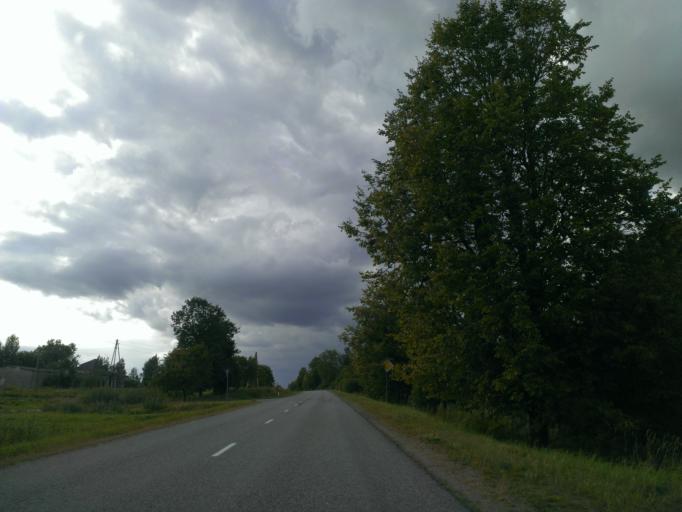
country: LV
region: Malpils
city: Malpils
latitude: 56.8937
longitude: 25.1755
